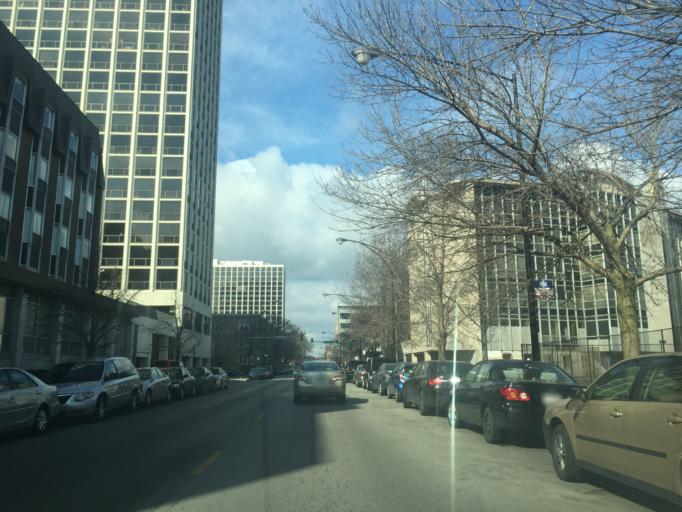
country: US
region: Illinois
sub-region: Cook County
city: Evanston
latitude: 41.9618
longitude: -87.6490
